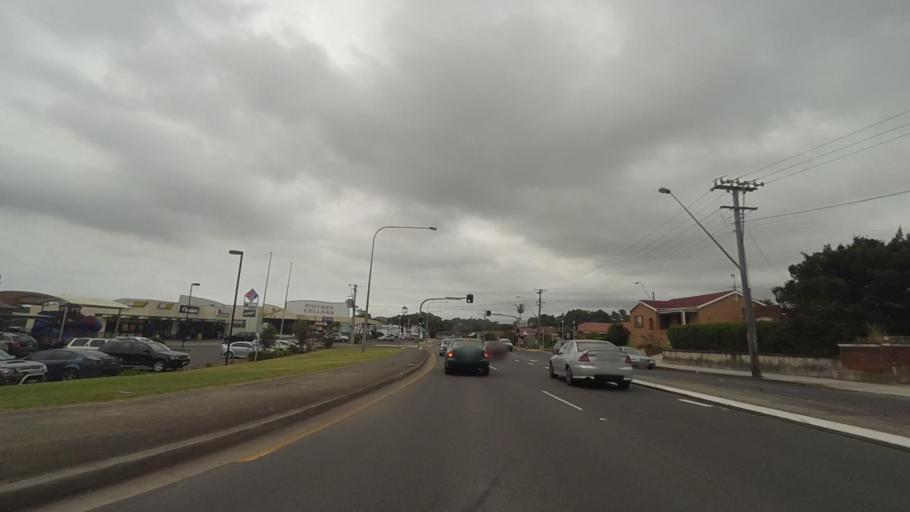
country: AU
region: New South Wales
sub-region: Wollongong
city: West Wollongong
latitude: -34.4317
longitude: 150.8659
